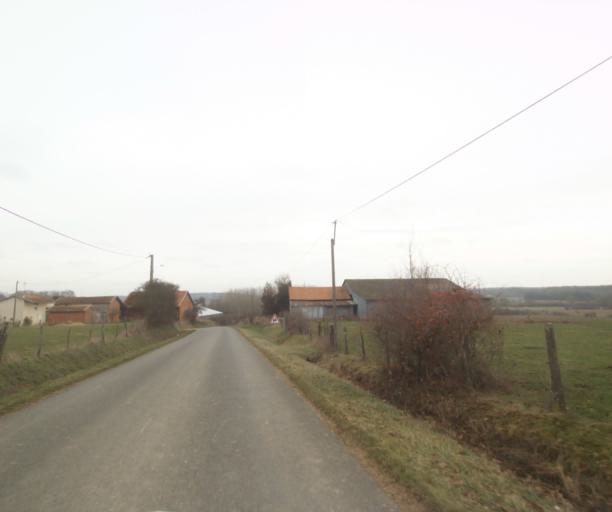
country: FR
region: Champagne-Ardenne
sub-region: Departement de la Marne
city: Pargny-sur-Saulx
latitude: 48.7413
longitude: 4.8367
